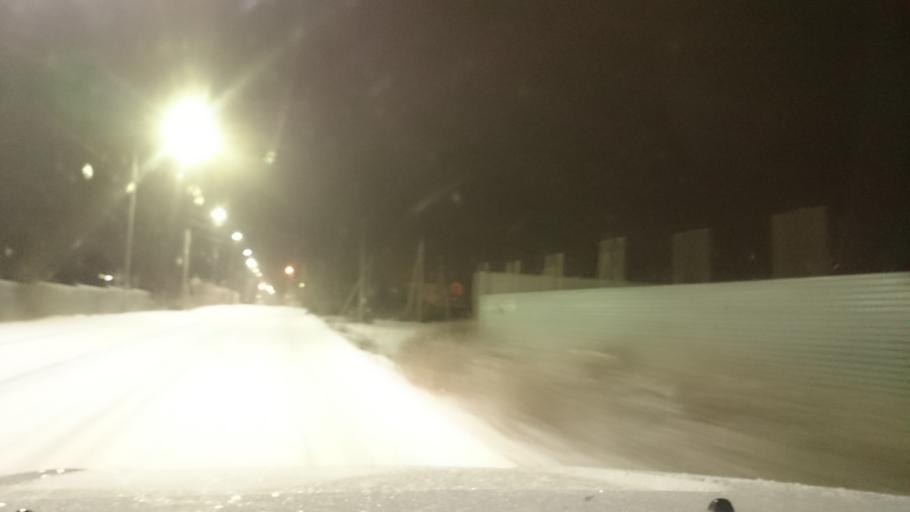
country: RU
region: Tula
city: Kosaya Gora
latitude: 54.1886
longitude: 37.5162
